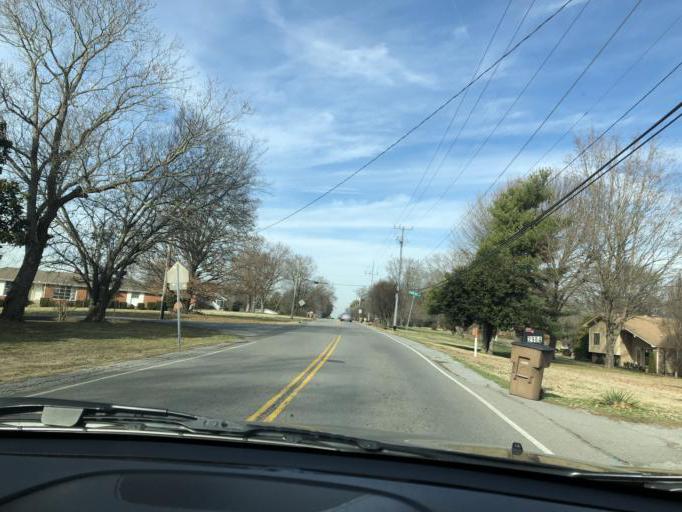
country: US
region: Tennessee
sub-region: Davidson County
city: Lakewood
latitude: 36.1964
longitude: -86.6736
